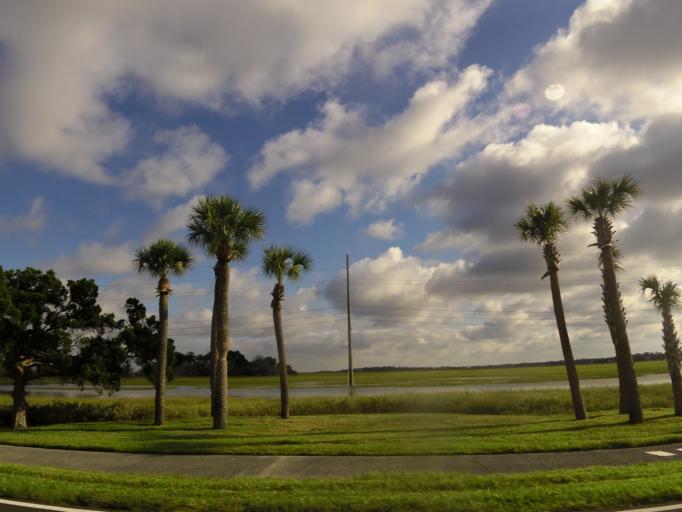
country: US
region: Georgia
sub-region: Glynn County
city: Saint Simons Island
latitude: 31.1812
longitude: -81.3625
